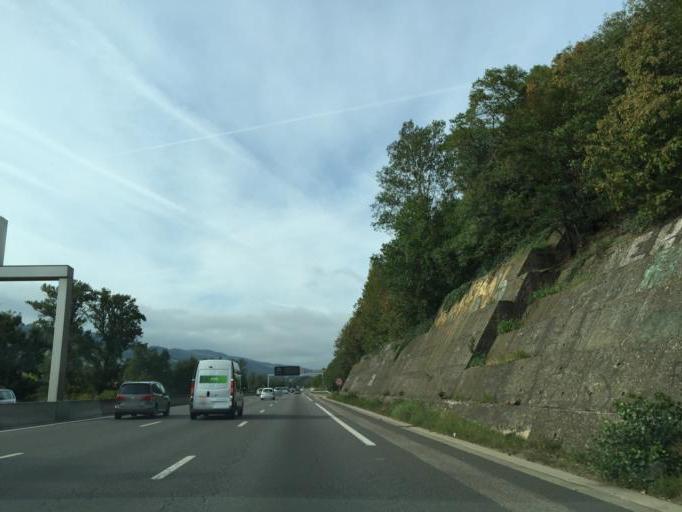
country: FR
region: Rhone-Alpes
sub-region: Departement de la Loire
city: Saint-Jean-Bonnefonds
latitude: 45.4544
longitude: 4.4798
